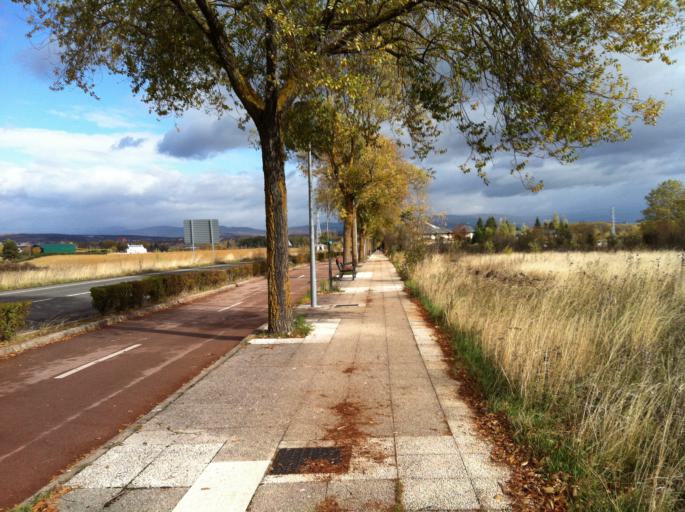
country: ES
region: Basque Country
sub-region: Provincia de Alava
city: Gasteiz / Vitoria
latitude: 42.8262
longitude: -2.6950
